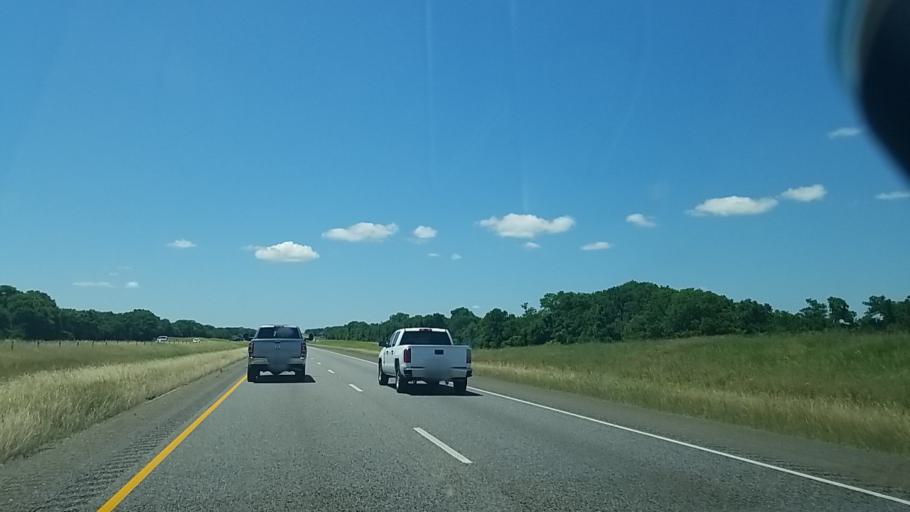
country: US
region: Texas
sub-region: Madison County
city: Madisonville
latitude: 30.9360
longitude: -95.8359
